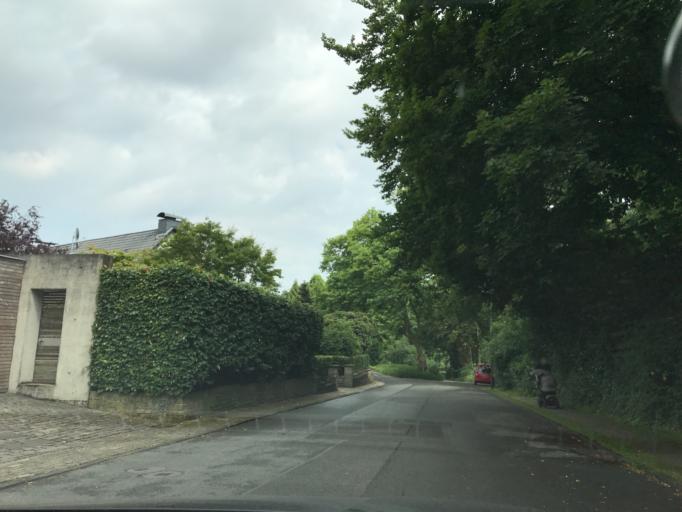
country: DE
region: North Rhine-Westphalia
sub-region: Regierungsbezirk Dusseldorf
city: Essen
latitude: 51.4127
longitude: 6.9969
